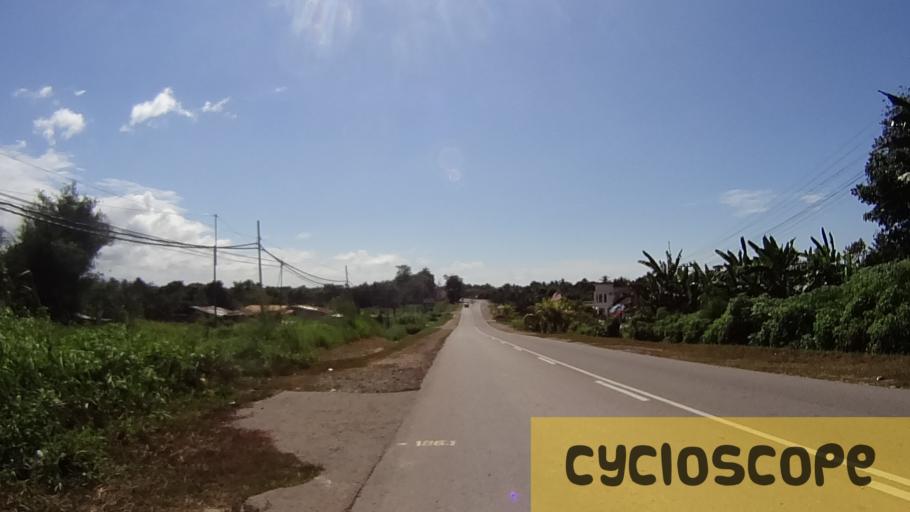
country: MY
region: Sabah
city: Beaufort
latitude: 5.1013
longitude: 115.5678
